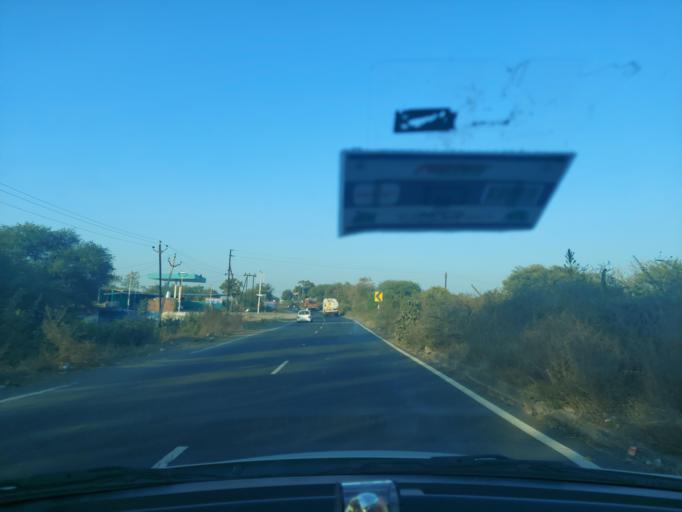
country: IN
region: Madhya Pradesh
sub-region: Indore
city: Sanwer
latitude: 23.0412
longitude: 75.8294
